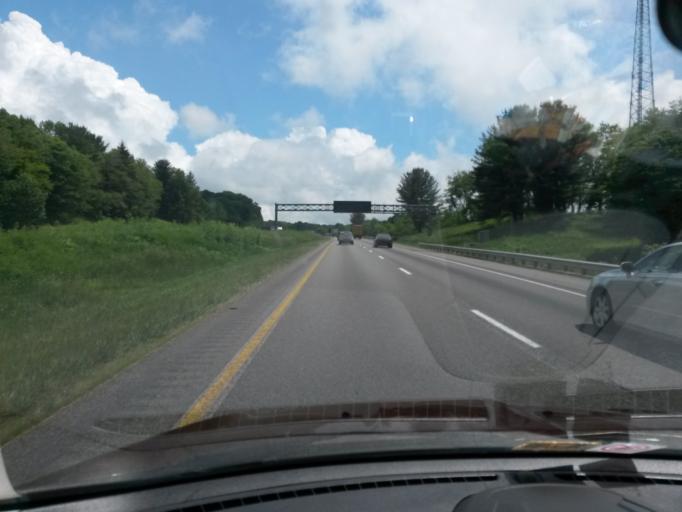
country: US
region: Virginia
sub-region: Carroll County
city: Hillsville
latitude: 36.7037
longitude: -80.7408
